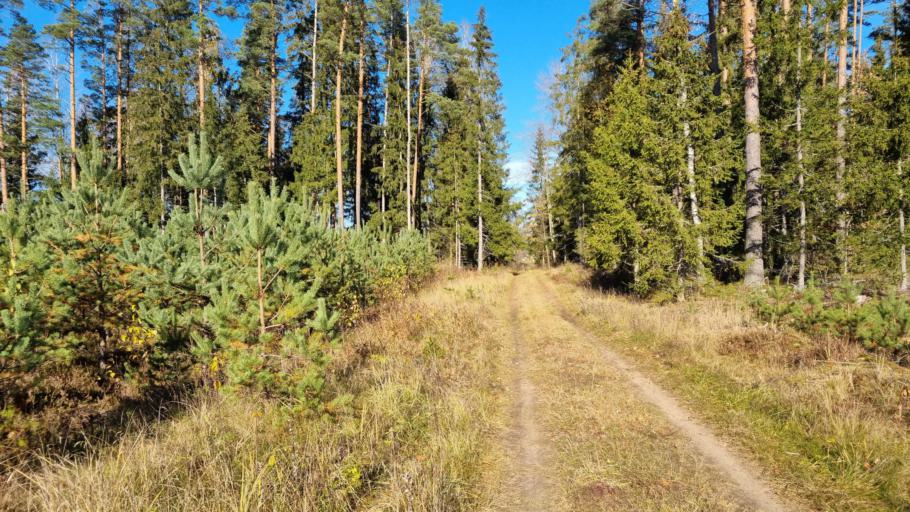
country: LV
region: Cesvaine
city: Cesvaine
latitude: 57.0812
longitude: 26.2963
